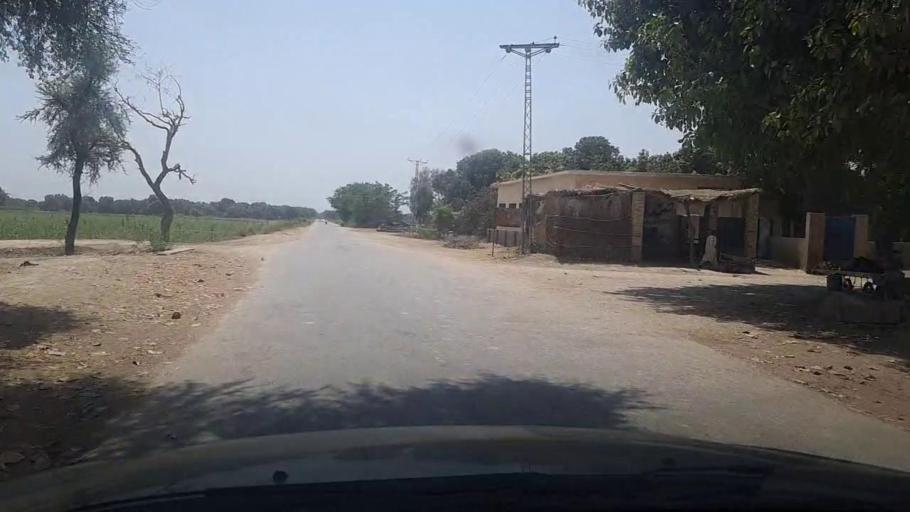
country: PK
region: Sindh
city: Tando Jam
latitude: 25.2962
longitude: 68.5868
